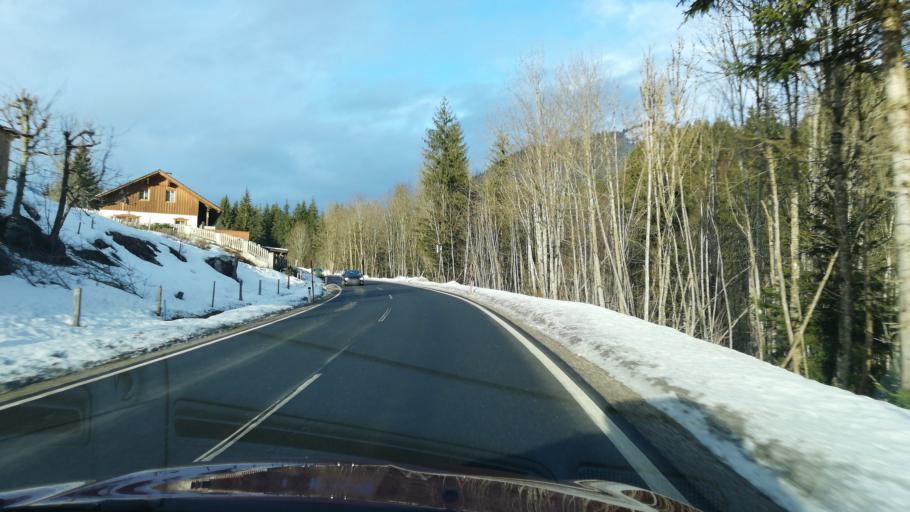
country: AT
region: Styria
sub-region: Politischer Bezirk Liezen
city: Liezen
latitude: 47.5840
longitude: 14.2736
